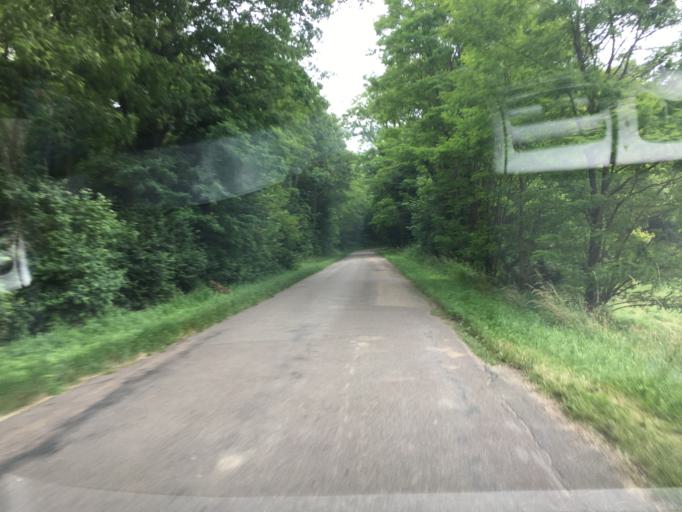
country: FR
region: Bourgogne
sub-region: Departement de l'Yonne
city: Fleury-la-Vallee
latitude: 47.8810
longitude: 3.4237
